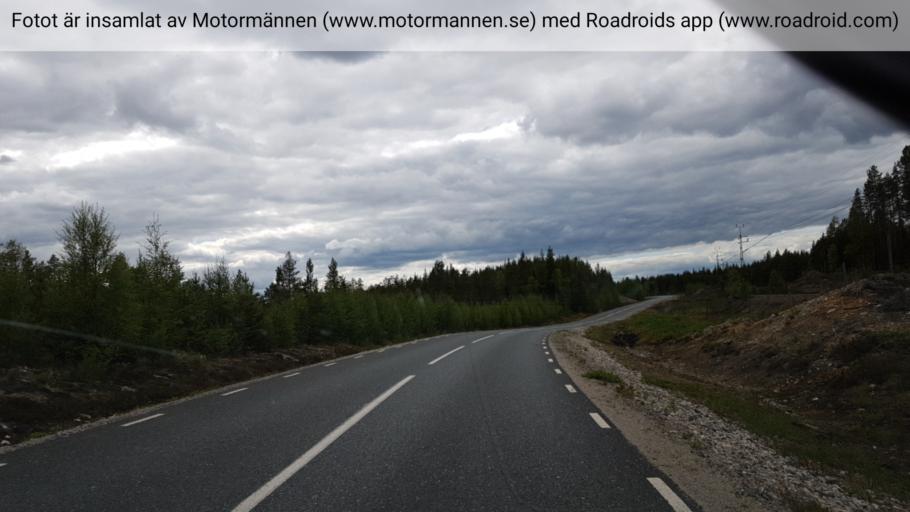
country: SE
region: Vaesterbotten
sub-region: Vindelns Kommun
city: Vindeln
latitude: 64.4400
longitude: 19.7415
